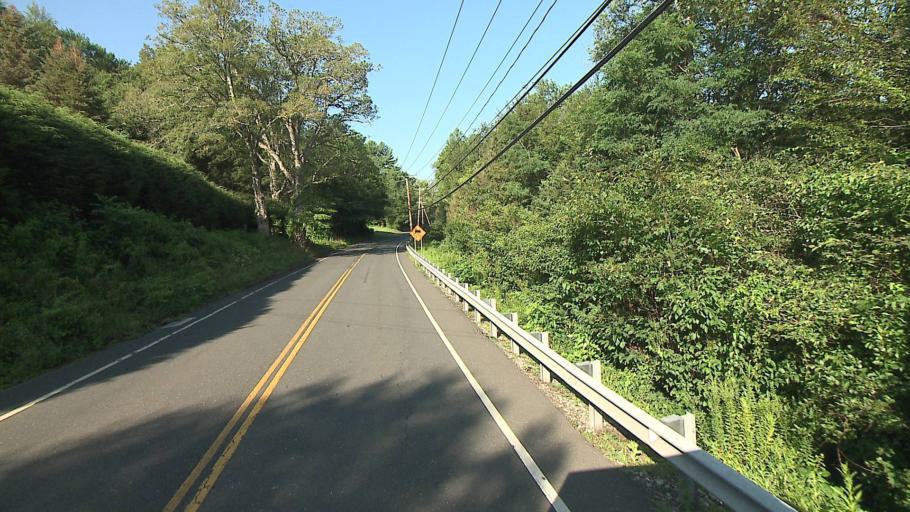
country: US
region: Connecticut
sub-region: Hartford County
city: Collinsville
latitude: 41.7794
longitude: -72.9328
